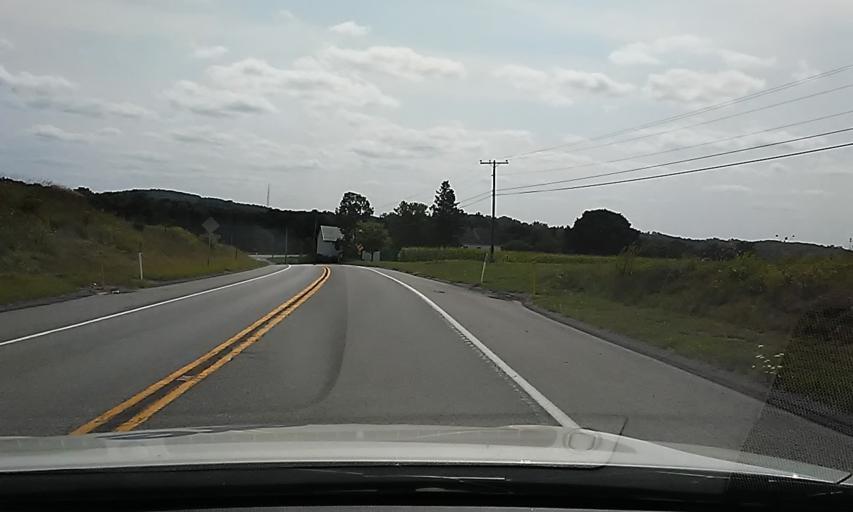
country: US
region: Pennsylvania
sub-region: Jefferson County
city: Punxsutawney
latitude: 40.8969
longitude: -79.0168
